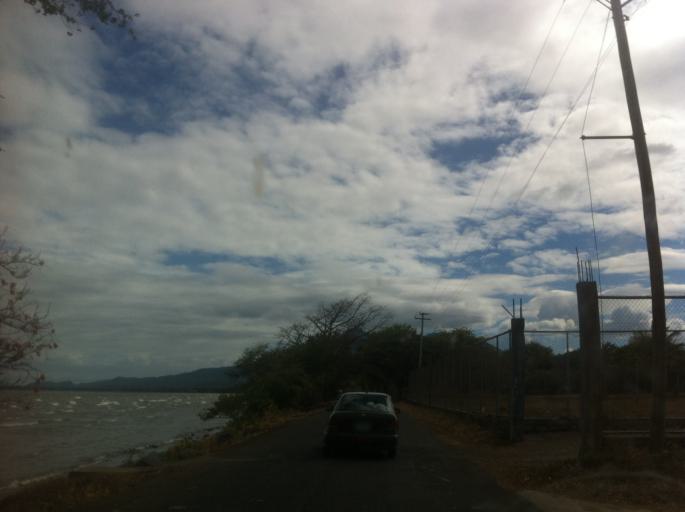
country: NI
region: Granada
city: Granada
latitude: 11.9561
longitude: -85.9453
